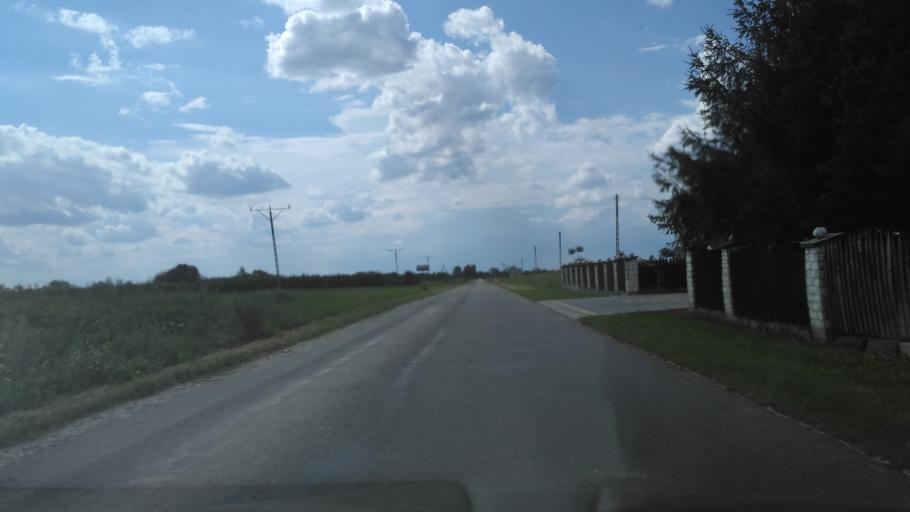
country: PL
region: Lublin Voivodeship
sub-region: Powiat leczynski
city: Milejow
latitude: 51.2152
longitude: 22.9167
